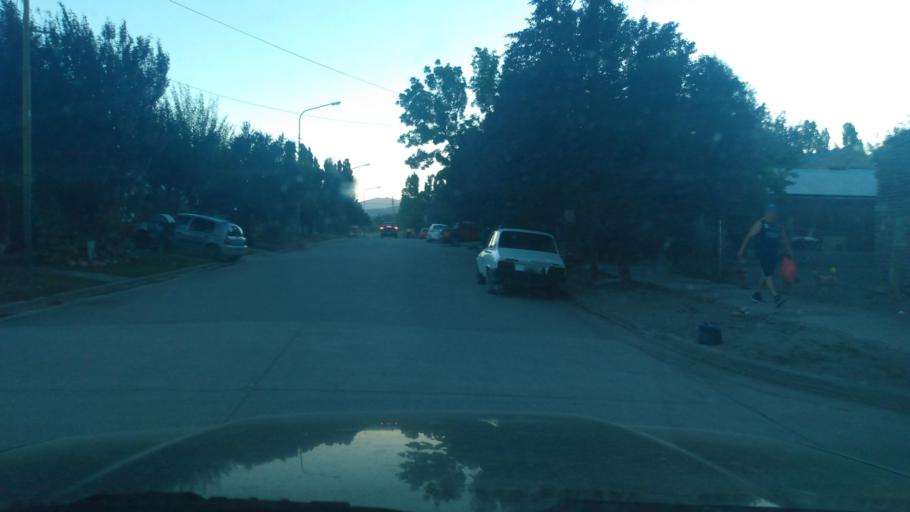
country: AR
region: Neuquen
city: Junin de los Andes
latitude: -39.9538
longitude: -71.0757
